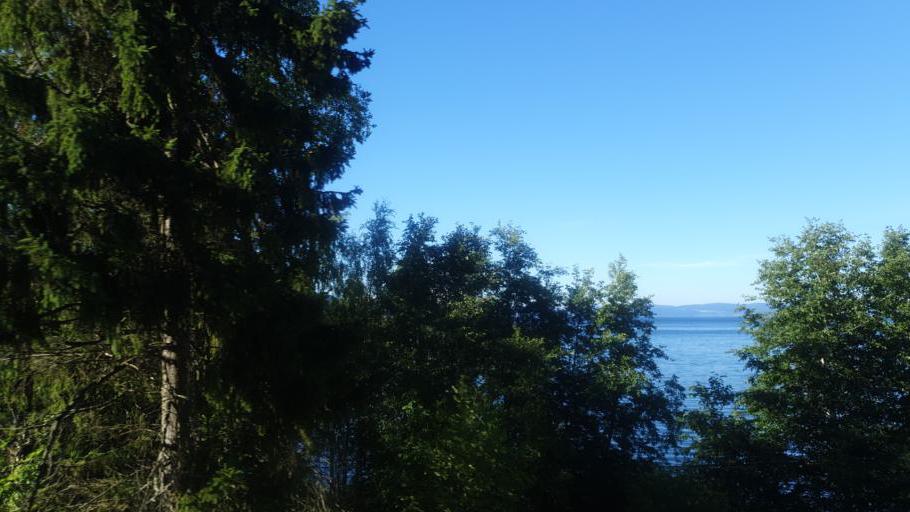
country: NO
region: Sor-Trondelag
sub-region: Skaun
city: Borsa
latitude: 63.3474
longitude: 9.9807
